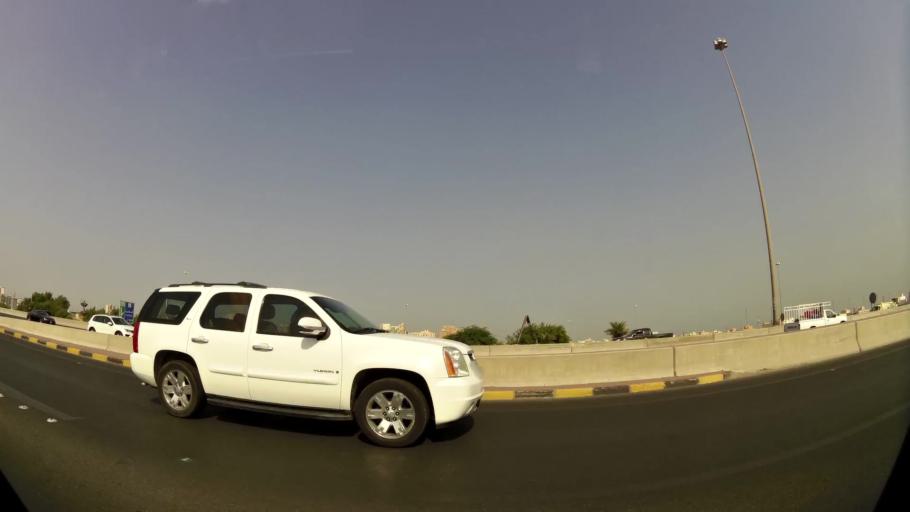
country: KW
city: Bayan
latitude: 29.3148
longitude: 48.0522
